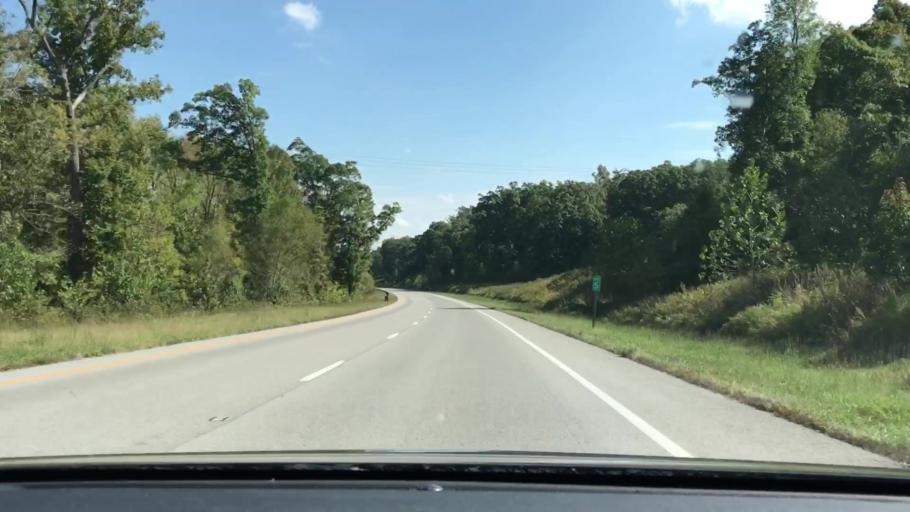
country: US
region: Kentucky
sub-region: Trigg County
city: Cadiz
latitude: 36.7843
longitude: -88.0360
